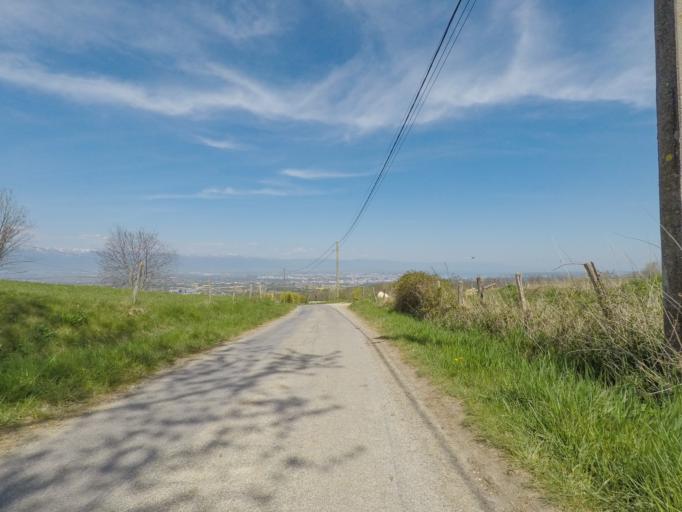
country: FR
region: Rhone-Alpes
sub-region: Departement de la Haute-Savoie
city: Archamps
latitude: 46.1214
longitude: 6.1377
